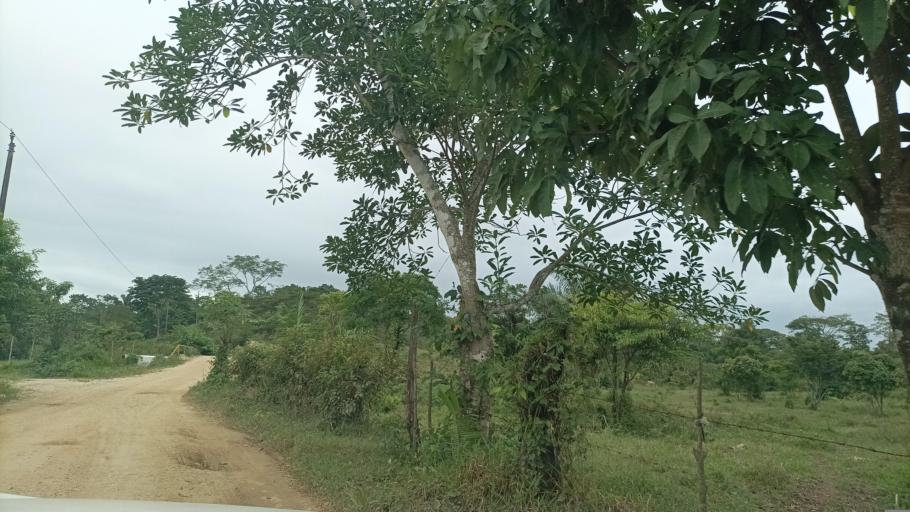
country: MX
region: Veracruz
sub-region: Uxpanapa
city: Poblado Cinco
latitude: 17.4824
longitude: -94.5730
